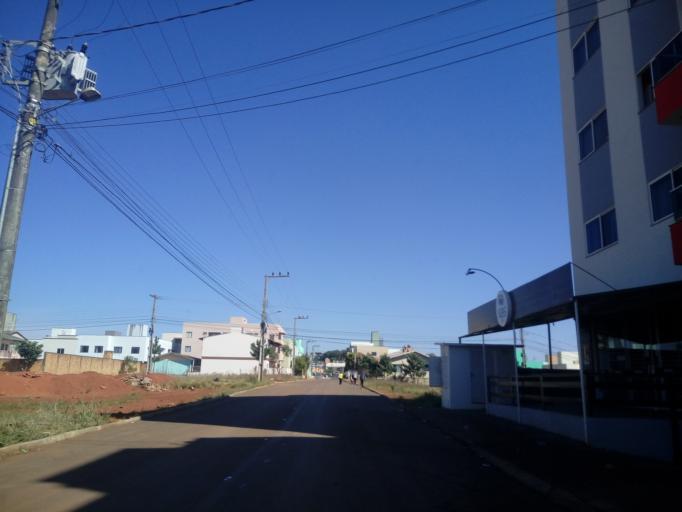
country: BR
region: Santa Catarina
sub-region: Chapeco
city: Chapeco
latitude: -27.0938
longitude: -52.6691
